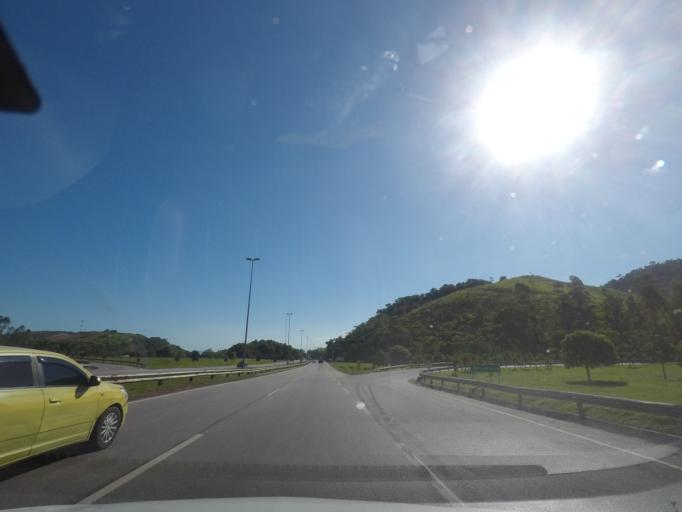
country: BR
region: Rio de Janeiro
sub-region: Guapimirim
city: Guapimirim
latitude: -22.6565
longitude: -43.0886
